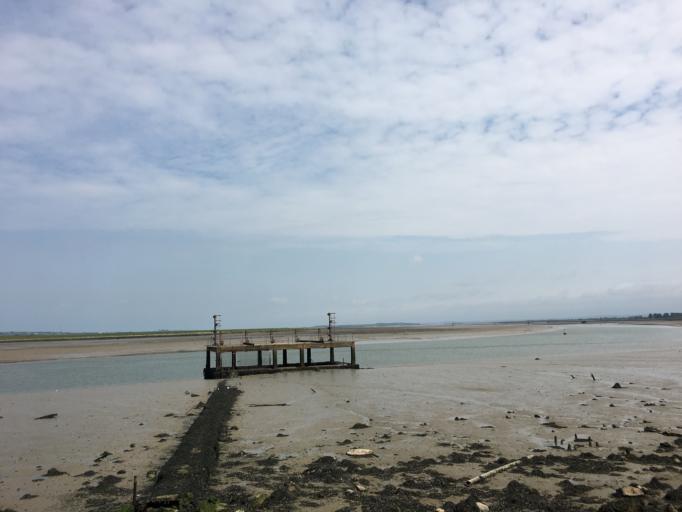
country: GB
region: England
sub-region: Kent
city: Sittingbourne
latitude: 51.3674
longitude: 0.7631
